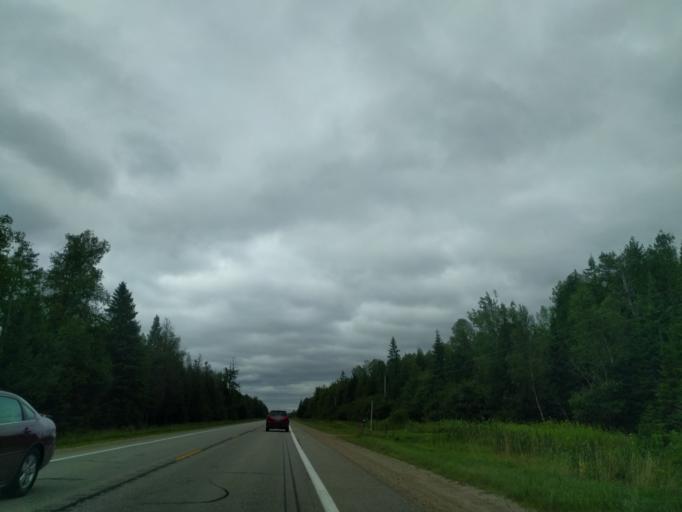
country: US
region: Michigan
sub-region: Delta County
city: Escanaba
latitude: 45.5735
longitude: -87.2506
